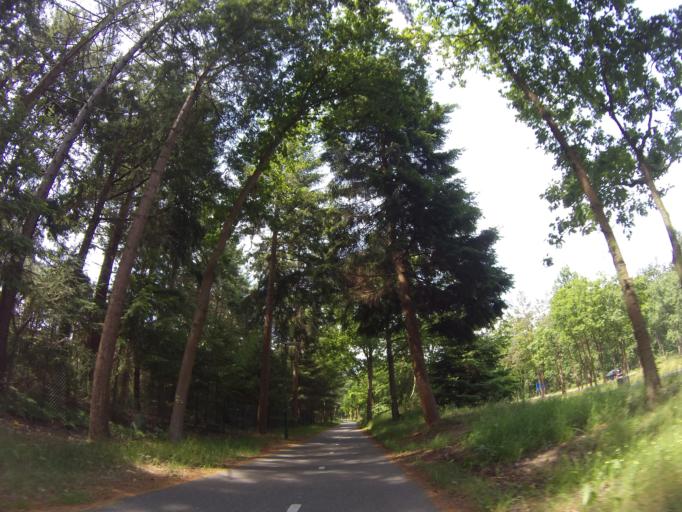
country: NL
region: Utrecht
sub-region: Gemeente Zeist
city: Zeist
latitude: 52.1057
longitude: 5.2171
